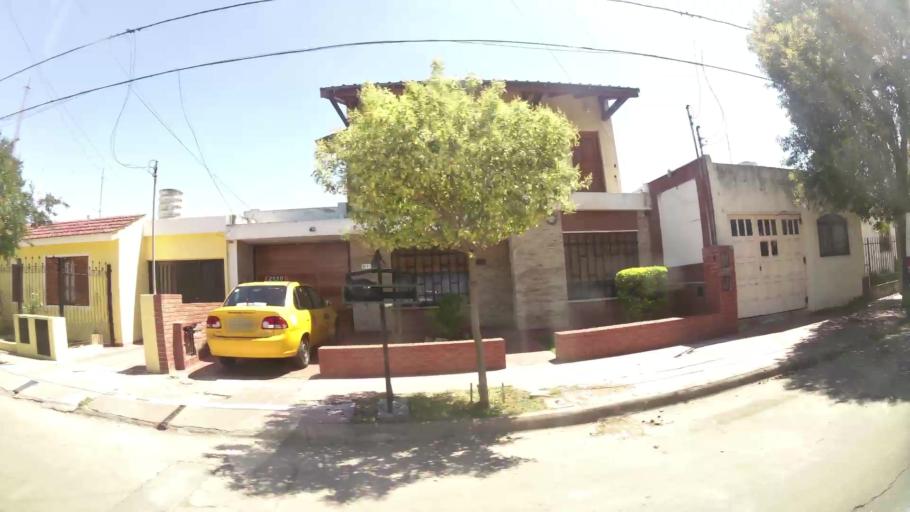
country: AR
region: Cordoba
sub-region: Departamento de Capital
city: Cordoba
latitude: -31.3821
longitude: -64.1694
